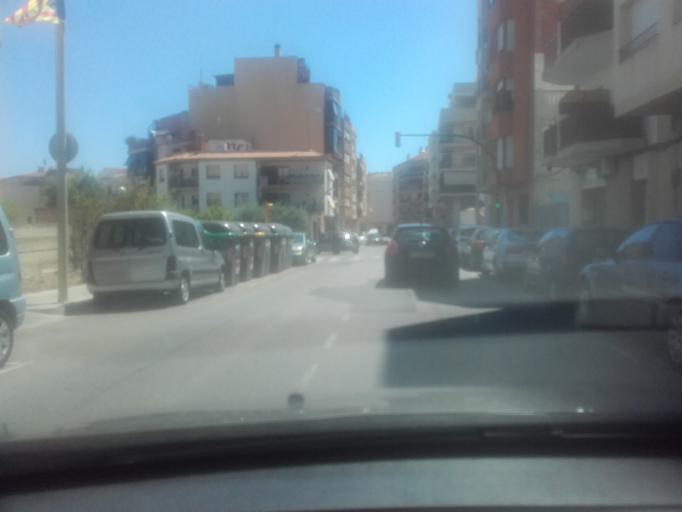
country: ES
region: Catalonia
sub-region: Provincia de Tarragona
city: El Vendrell
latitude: 41.2201
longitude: 1.5280
